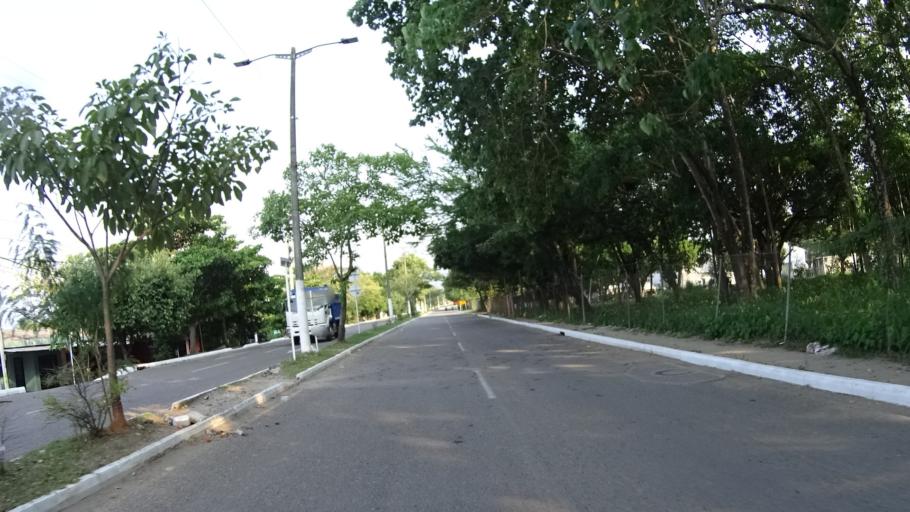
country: CO
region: Cundinamarca
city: Puerto Salgar
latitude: 5.4756
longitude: -74.6694
